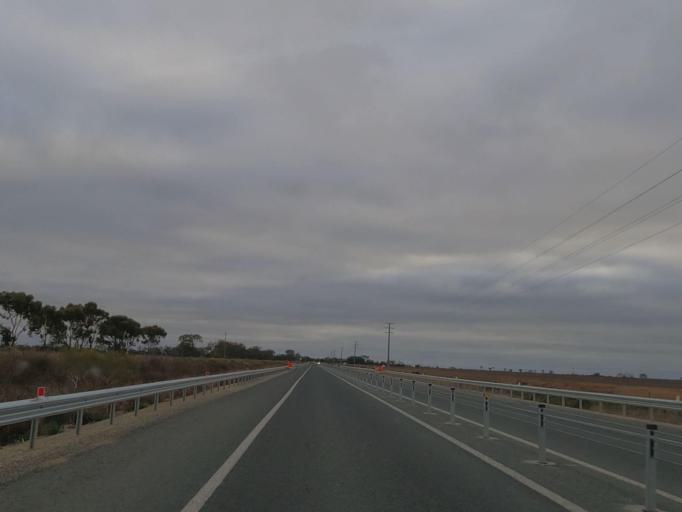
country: AU
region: Victoria
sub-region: Swan Hill
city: Swan Hill
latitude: -35.5431
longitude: 143.7564
